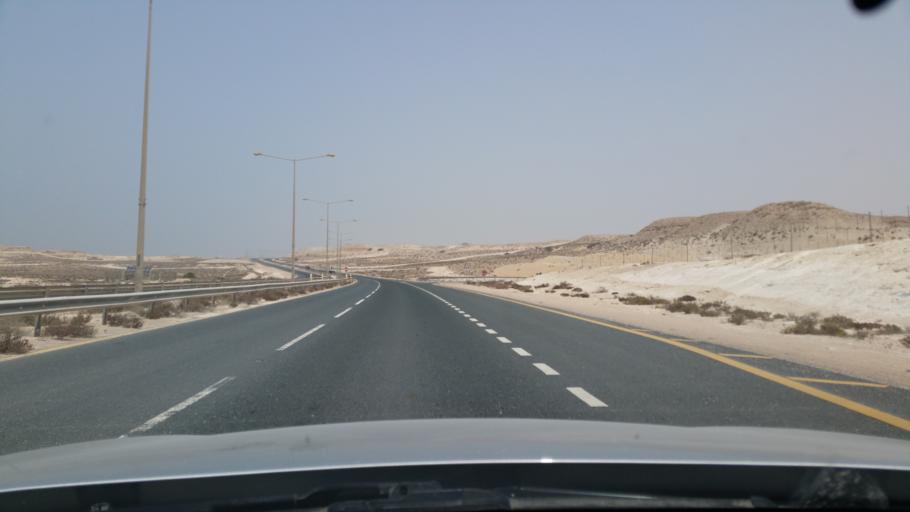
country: QA
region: Baladiyat ar Rayyan
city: Dukhan
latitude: 25.3445
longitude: 50.7831
